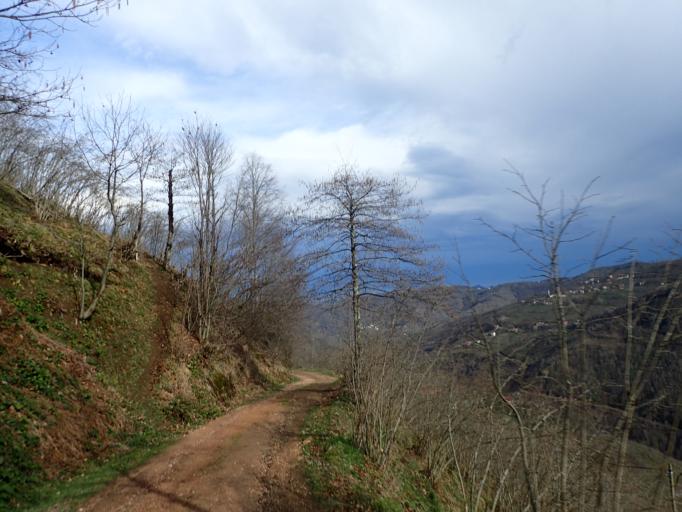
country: TR
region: Ordu
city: Camas
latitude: 40.8876
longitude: 37.5804
